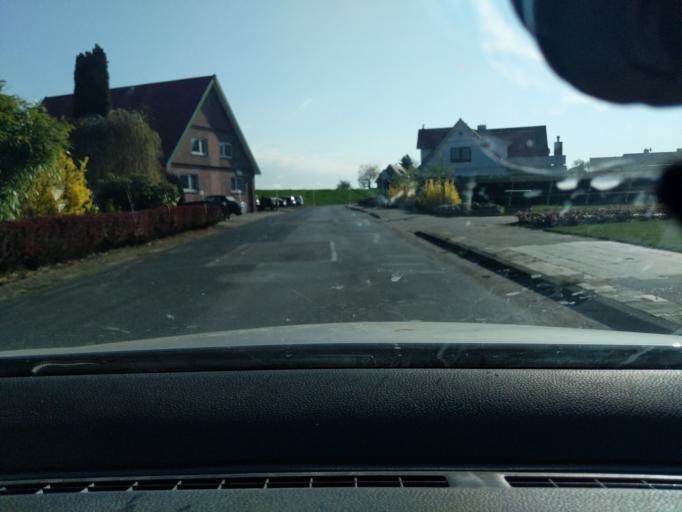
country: DE
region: Lower Saxony
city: Grunendeich
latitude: 53.5653
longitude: 9.6310
